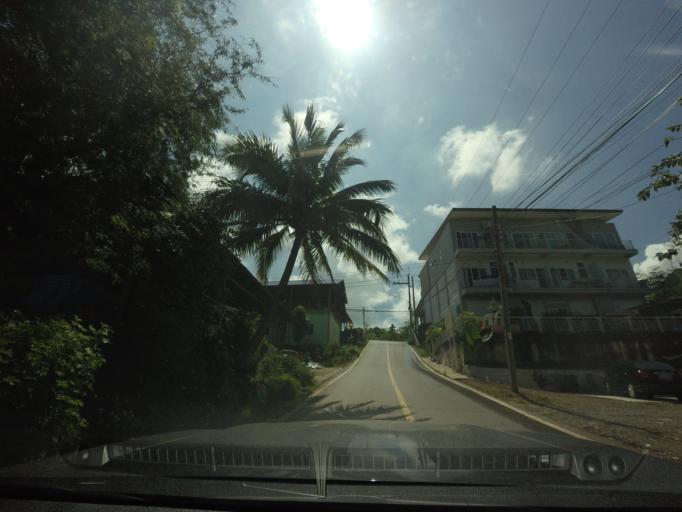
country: TH
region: Phetchabun
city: Khao Kho
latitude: 16.7705
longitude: 101.0479
